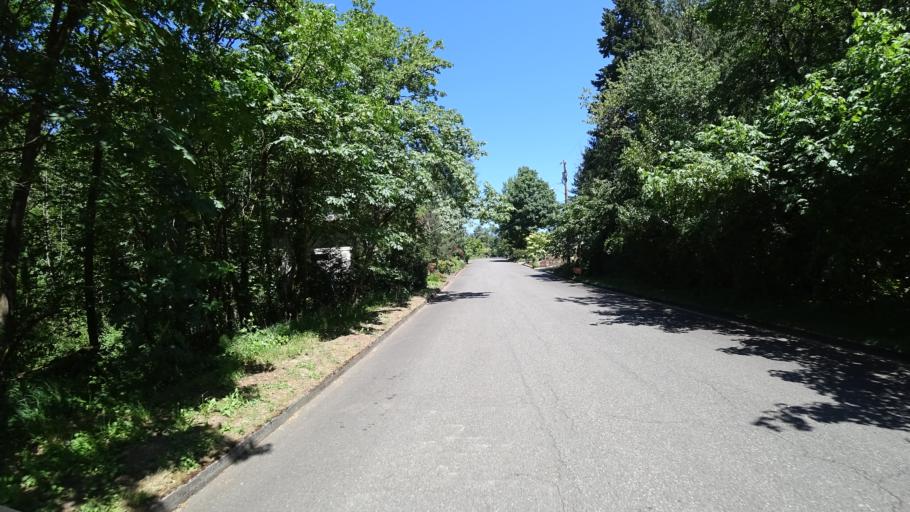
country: US
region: Oregon
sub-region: Washington County
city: Raleigh Hills
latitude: 45.4862
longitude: -122.7182
